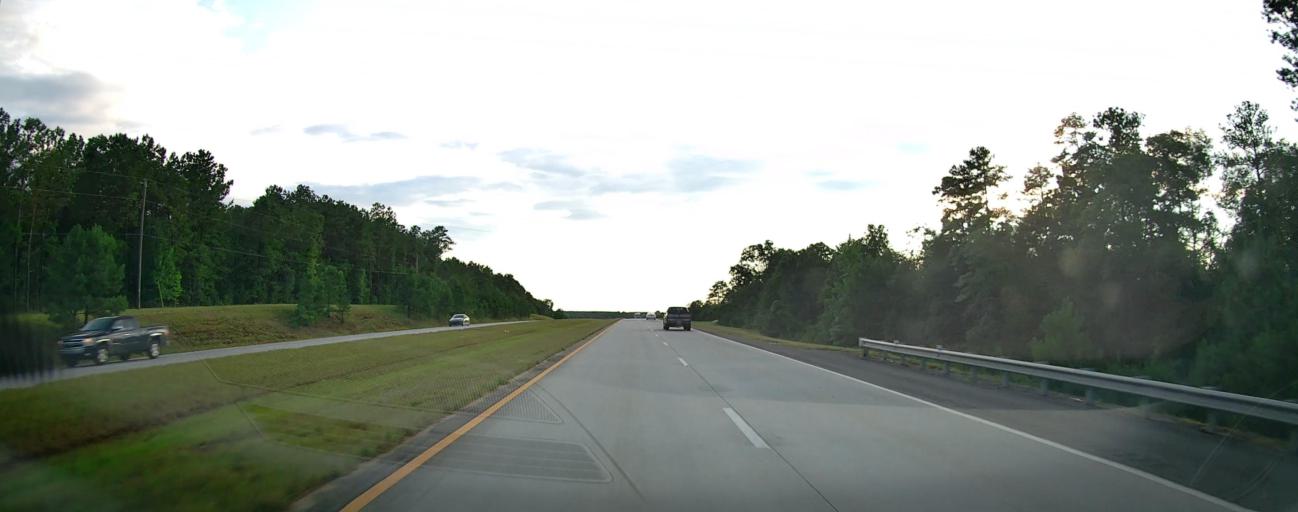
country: US
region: Georgia
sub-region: Peach County
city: Fort Valley
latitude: 32.5547
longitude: -83.9626
